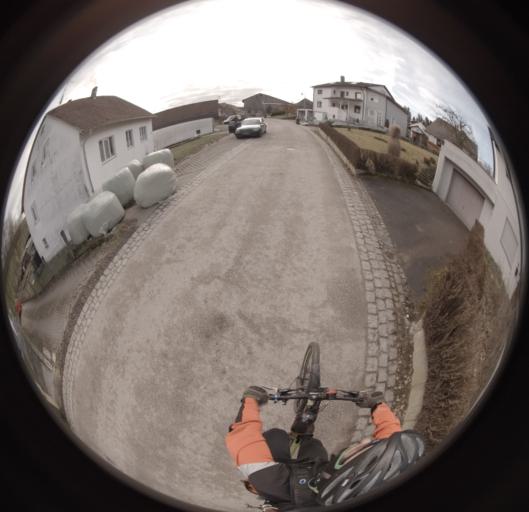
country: DE
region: Baden-Wuerttemberg
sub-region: Regierungsbezirk Stuttgart
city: Ottenbach
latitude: 48.7242
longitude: 9.7333
